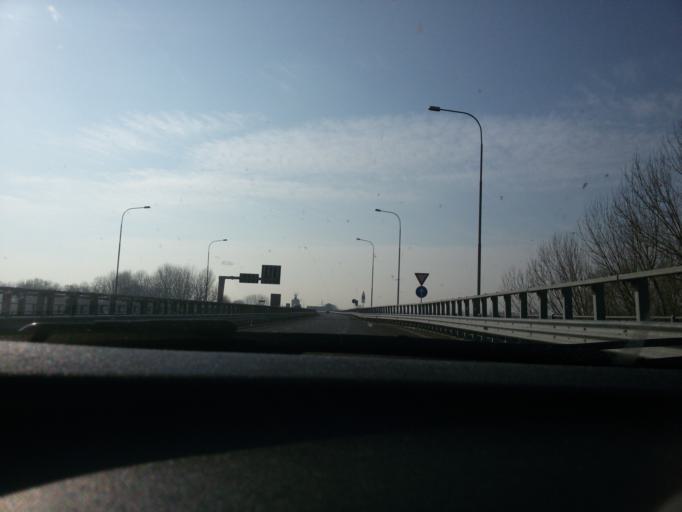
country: IT
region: Piedmont
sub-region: Provincia di Alessandria
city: Valle San Bartolomeo
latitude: 44.9347
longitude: 8.6219
